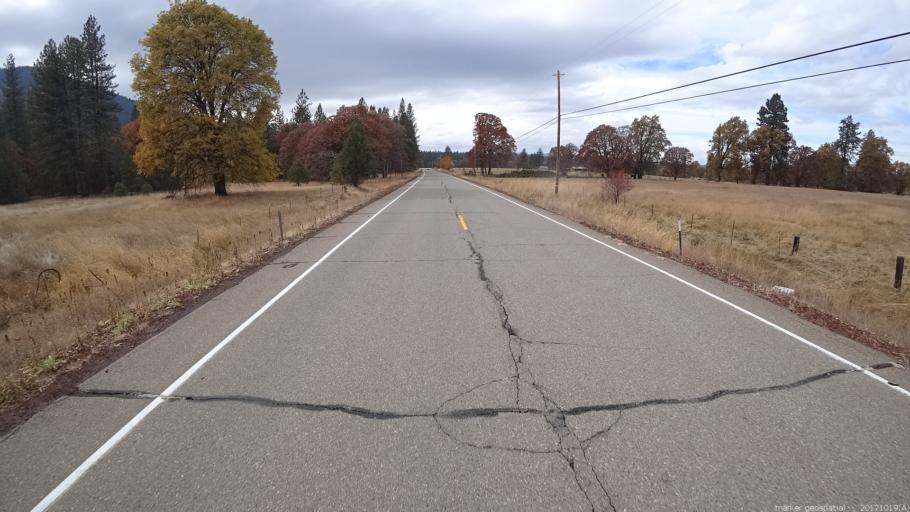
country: US
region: California
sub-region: Shasta County
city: Burney
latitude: 41.0944
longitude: -121.5419
